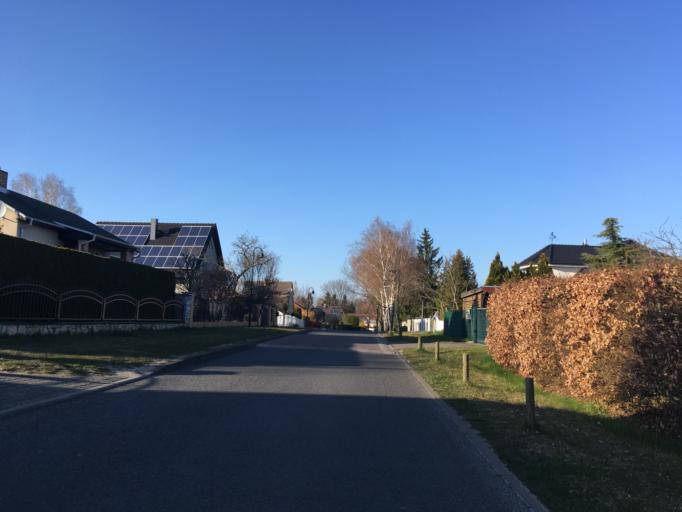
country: DE
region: Berlin
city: Buch
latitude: 52.6359
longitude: 13.5229
